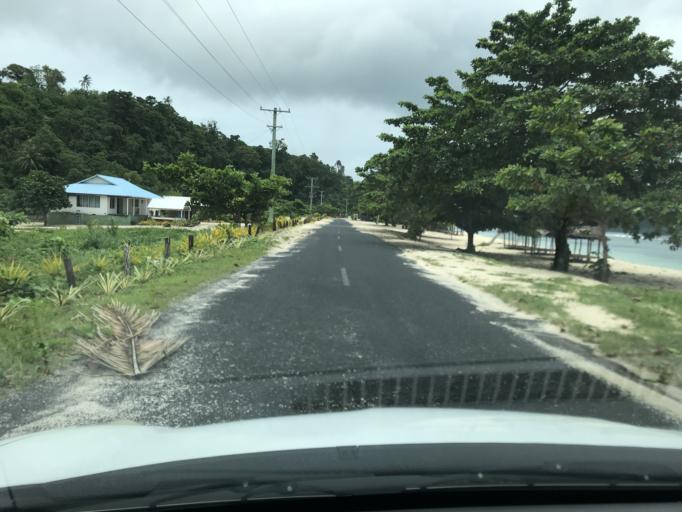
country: WS
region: Va`a-o-Fonoti
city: Samamea
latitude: -14.0457
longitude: -171.4484
